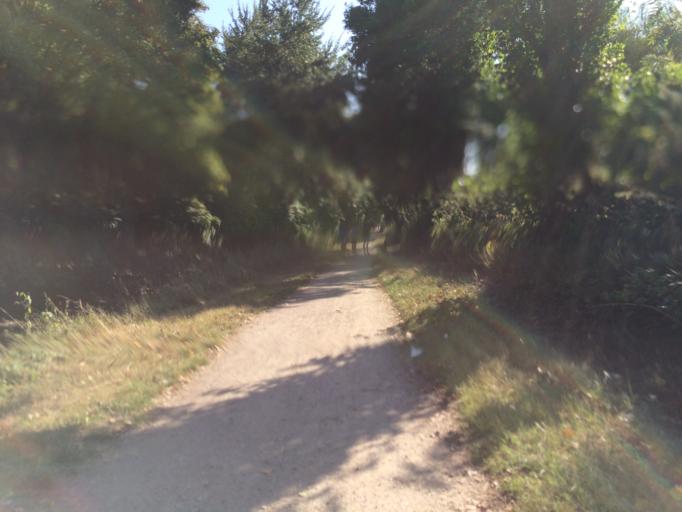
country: FR
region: Ile-de-France
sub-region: Departement de l'Essonne
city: Epinay-sur-Orge
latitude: 48.6679
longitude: 2.3200
